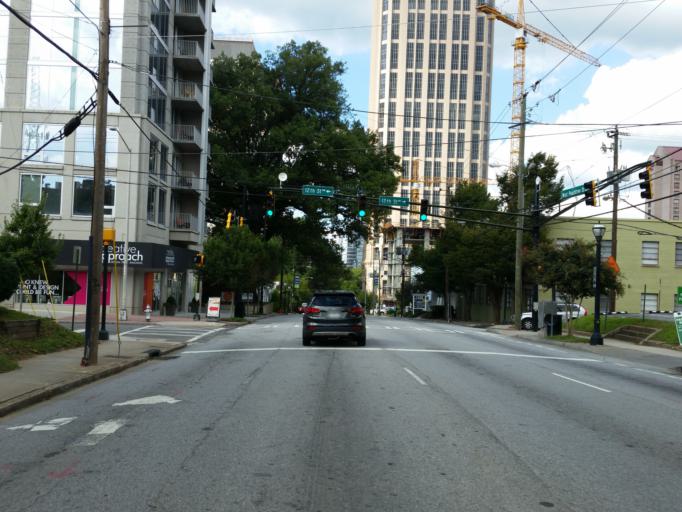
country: US
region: Georgia
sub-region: Fulton County
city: Atlanta
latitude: 33.7841
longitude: -84.3878
